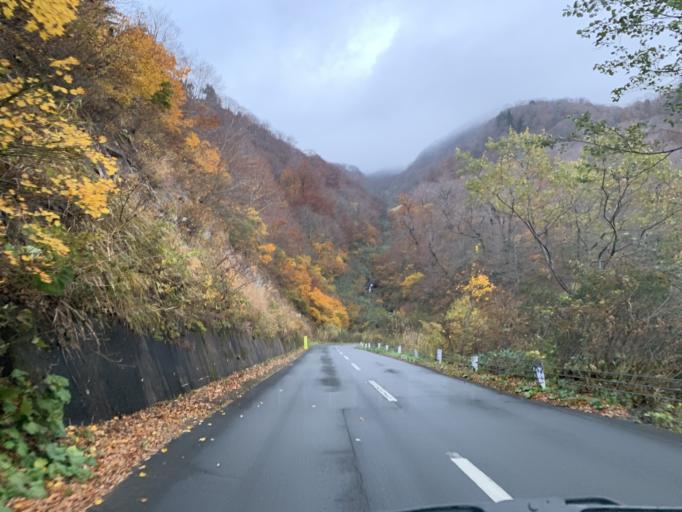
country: JP
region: Iwate
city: Mizusawa
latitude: 39.1266
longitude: 140.8245
